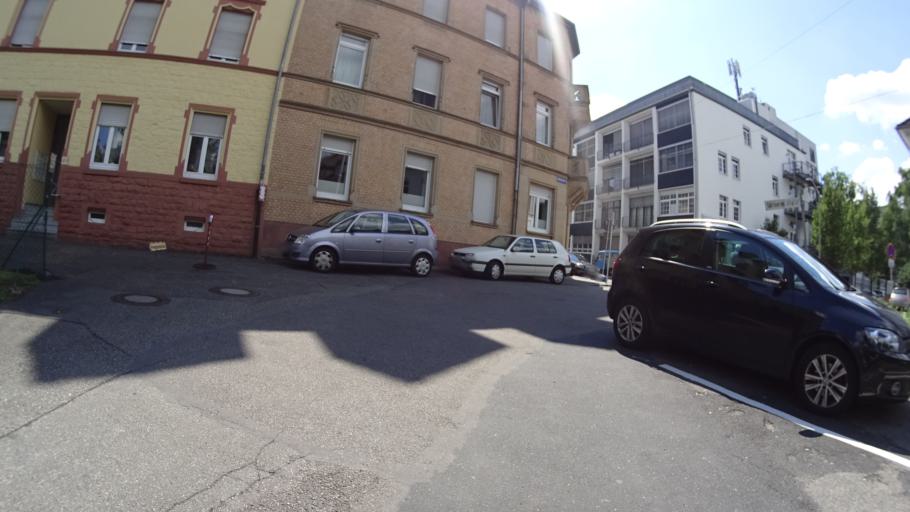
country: DE
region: Baden-Wuerttemberg
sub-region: Karlsruhe Region
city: Karlsruhe
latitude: 48.9975
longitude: 8.4653
